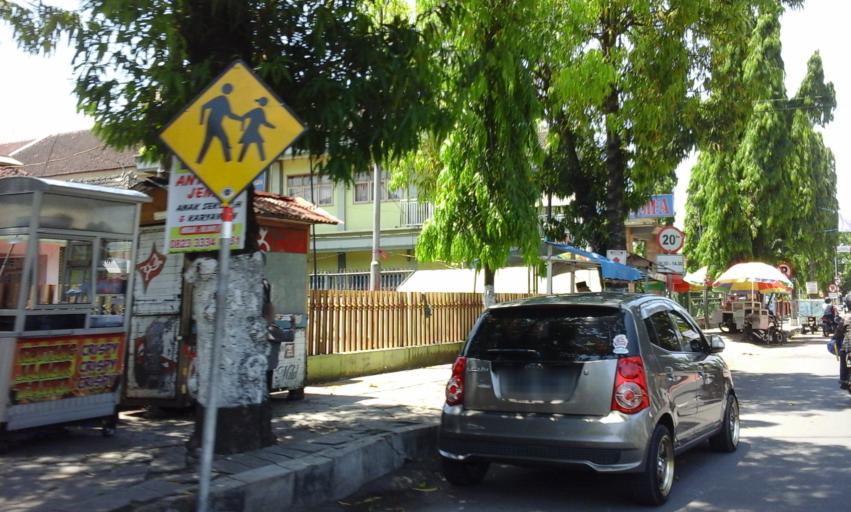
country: ID
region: East Java
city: Krajan
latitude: -8.1623
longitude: 113.7076
